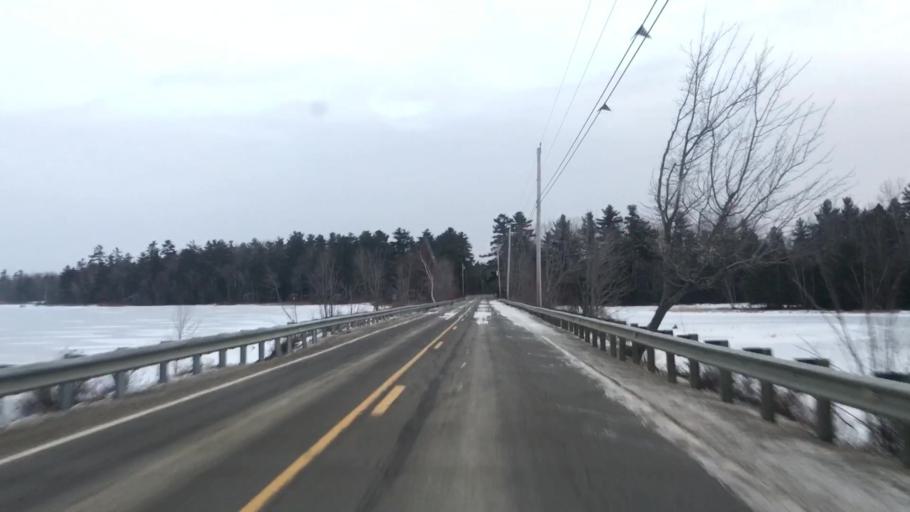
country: US
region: Maine
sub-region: Hancock County
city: Ellsworth
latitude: 44.6138
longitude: -68.3869
